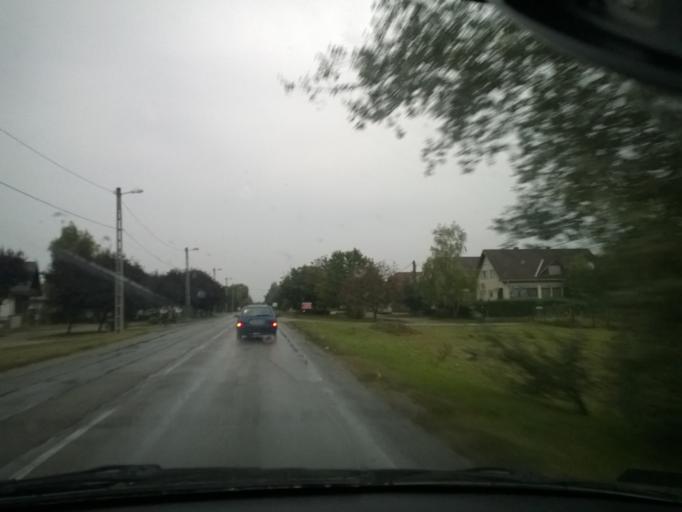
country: HU
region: Pest
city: Kiskunlachaza
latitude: 47.1663
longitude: 19.0001
